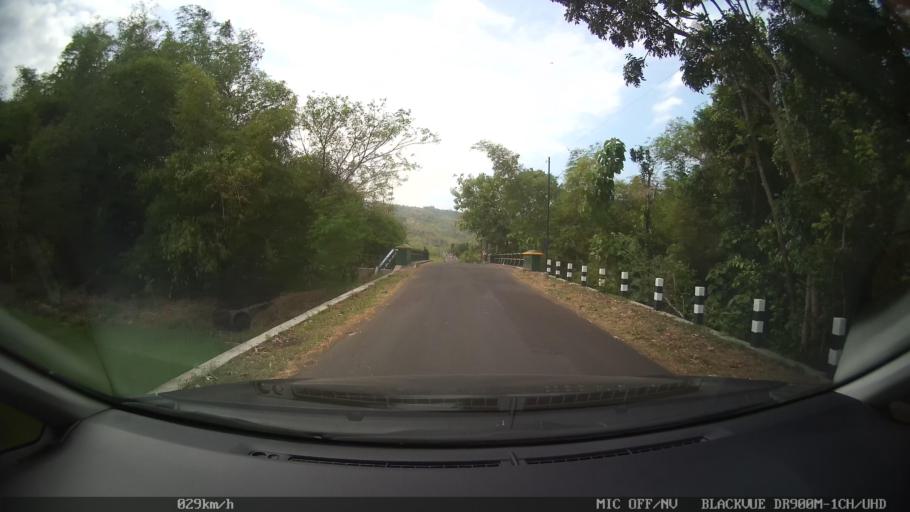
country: ID
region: Central Java
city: Candi Prambanan
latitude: -7.8111
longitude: 110.5034
